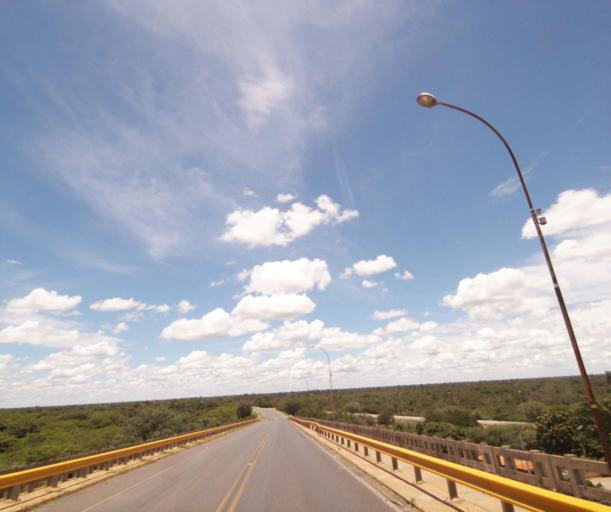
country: BR
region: Bahia
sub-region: Bom Jesus Da Lapa
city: Bom Jesus da Lapa
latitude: -13.2567
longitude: -43.4364
